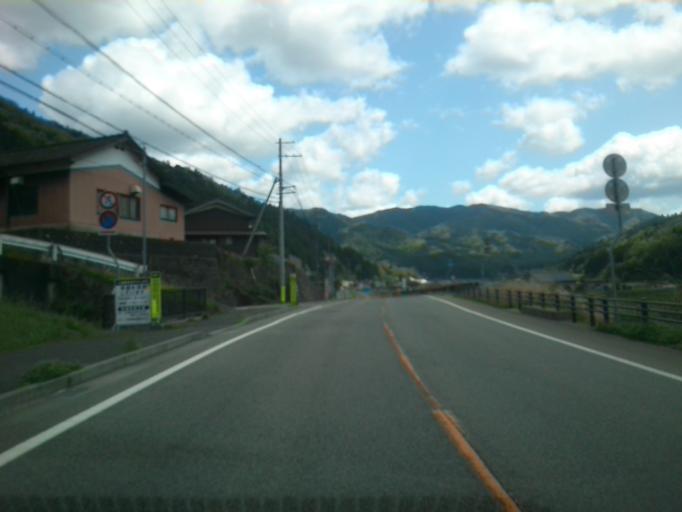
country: JP
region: Kyoto
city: Fukuchiyama
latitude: 35.4280
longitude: 135.0049
